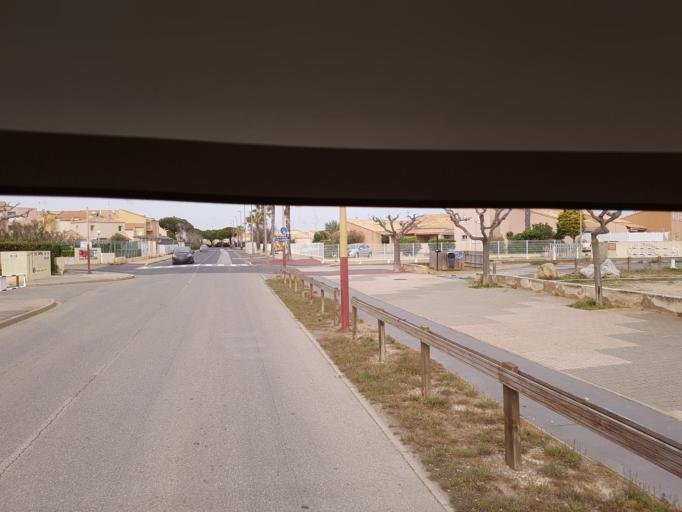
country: FR
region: Languedoc-Roussillon
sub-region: Departement de l'Aude
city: Fleury
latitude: 43.1829
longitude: 3.1946
